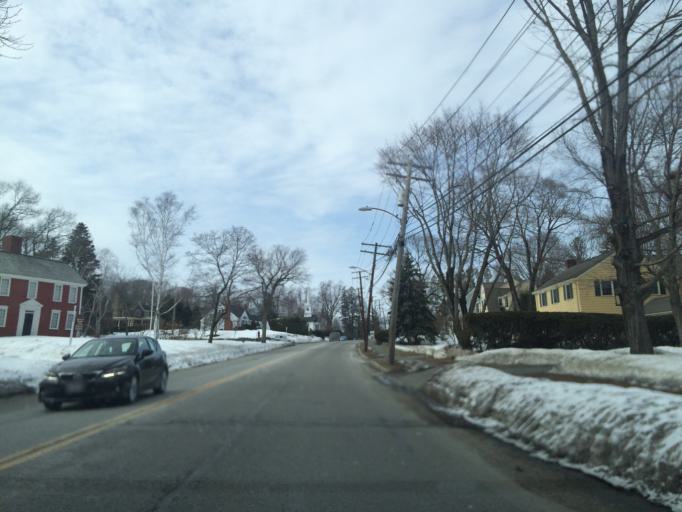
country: US
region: Massachusetts
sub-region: Middlesex County
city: Lexington
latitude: 42.4412
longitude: -71.2155
